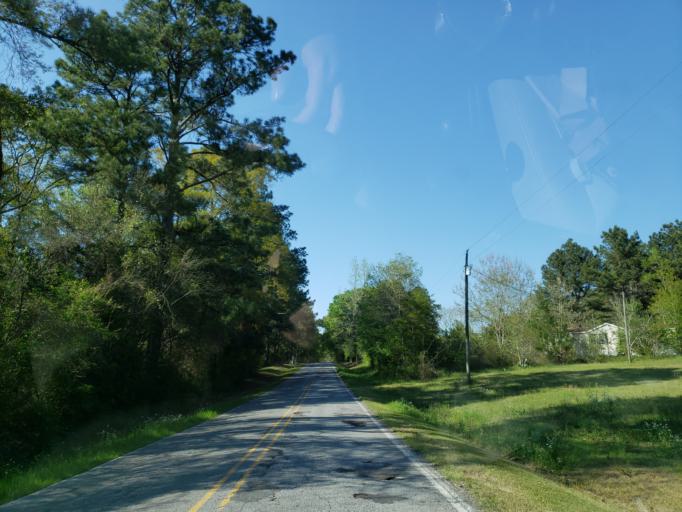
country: US
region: Mississippi
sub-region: Forrest County
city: Rawls Springs
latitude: 31.5274
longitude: -89.3592
